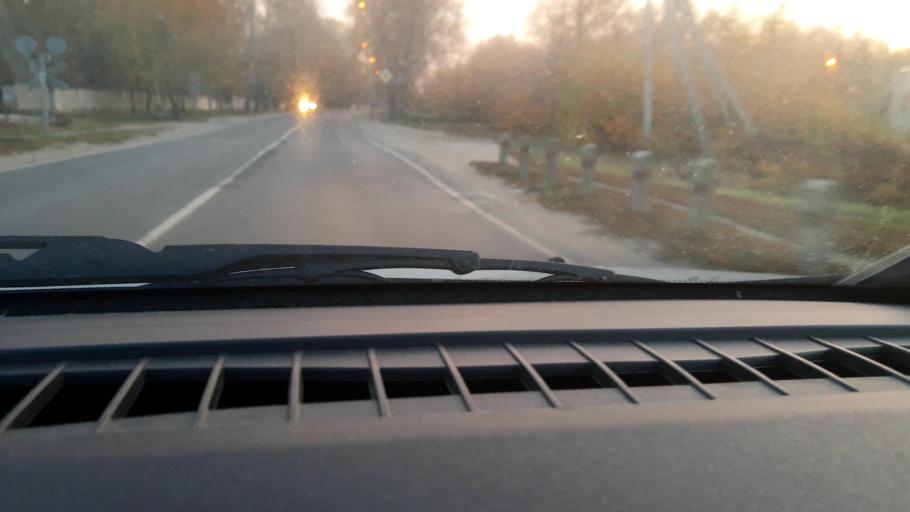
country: RU
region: Nizjnij Novgorod
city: Bor
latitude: 56.3786
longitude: 44.0320
